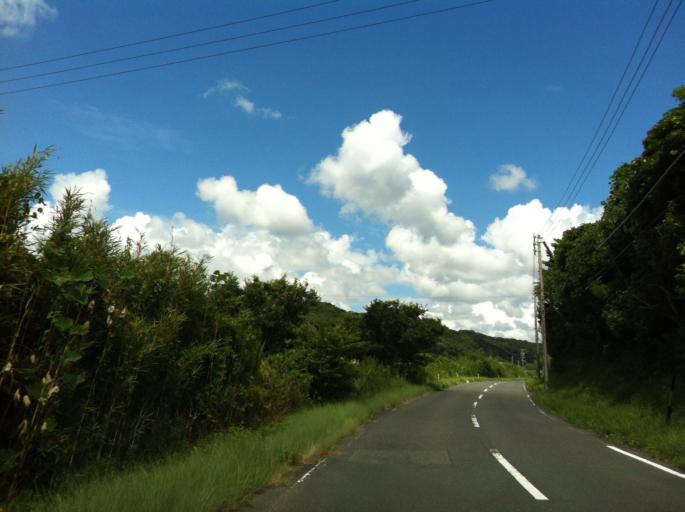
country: JP
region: Shizuoka
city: Kakegawa
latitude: 34.6881
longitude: 137.9879
